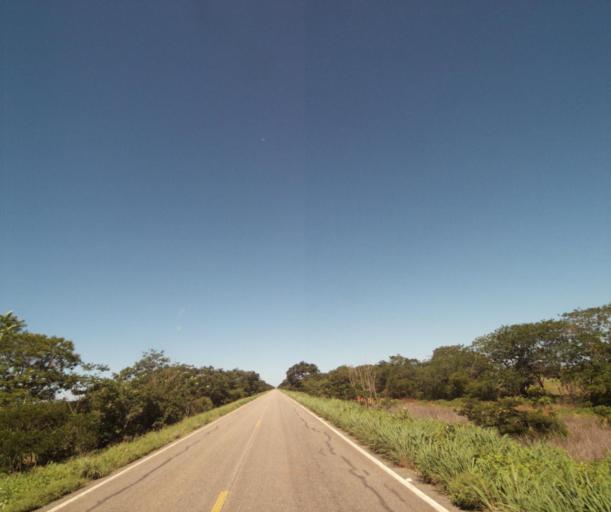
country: BR
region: Bahia
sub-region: Palmas De Monte Alto
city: Palmas de Monte Alto
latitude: -14.2624
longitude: -43.3202
